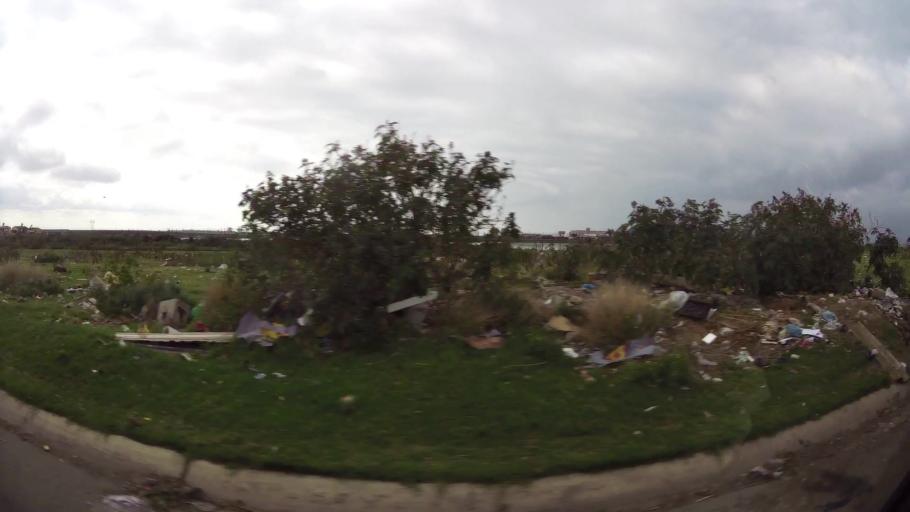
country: ZA
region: Eastern Cape
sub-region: Nelson Mandela Bay Metropolitan Municipality
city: Port Elizabeth
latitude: -33.8788
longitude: 25.6013
